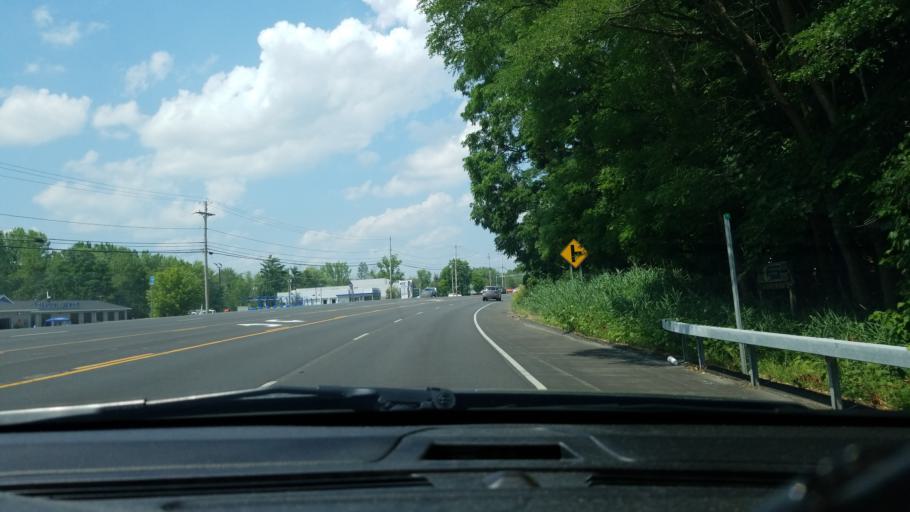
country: US
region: New York
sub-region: Onondaga County
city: Liverpool
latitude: 43.1469
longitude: -76.2302
